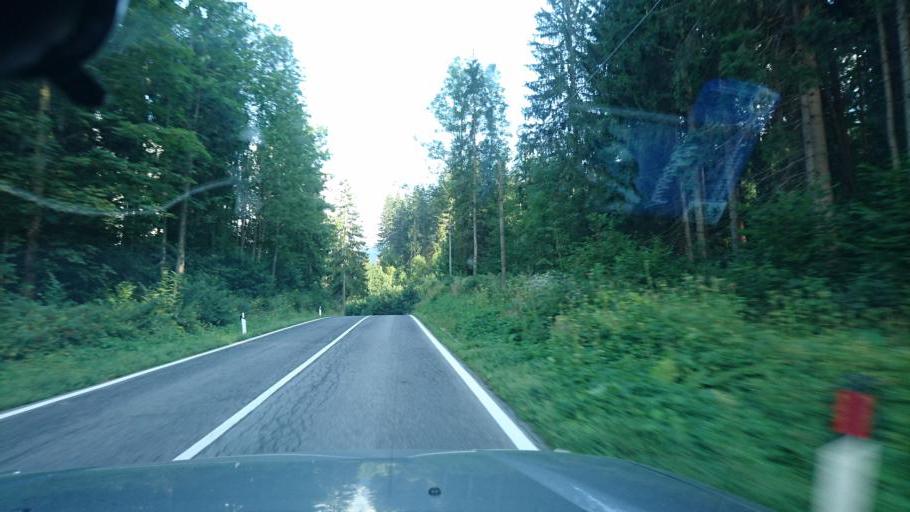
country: IT
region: Friuli Venezia Giulia
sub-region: Provincia di Udine
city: Tarvisio
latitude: 46.5017
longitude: 13.6258
